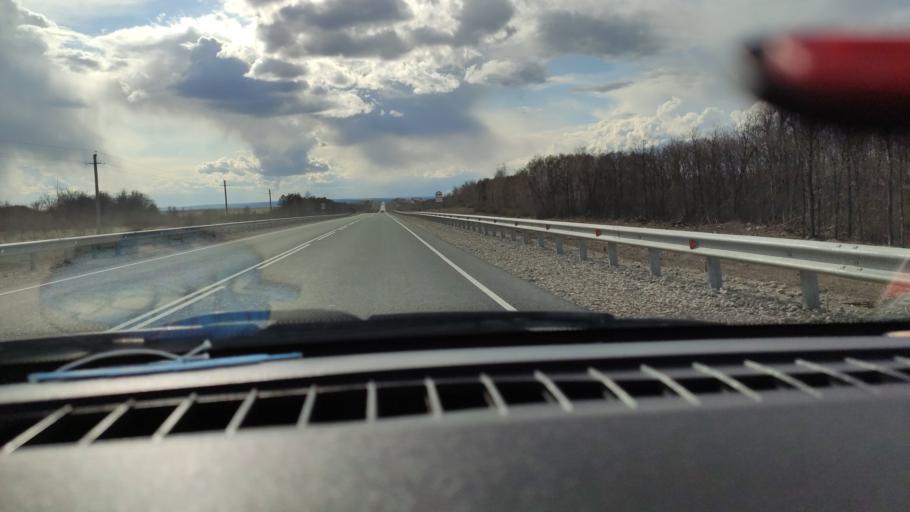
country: RU
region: Saratov
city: Shikhany
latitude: 52.1611
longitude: 47.1494
